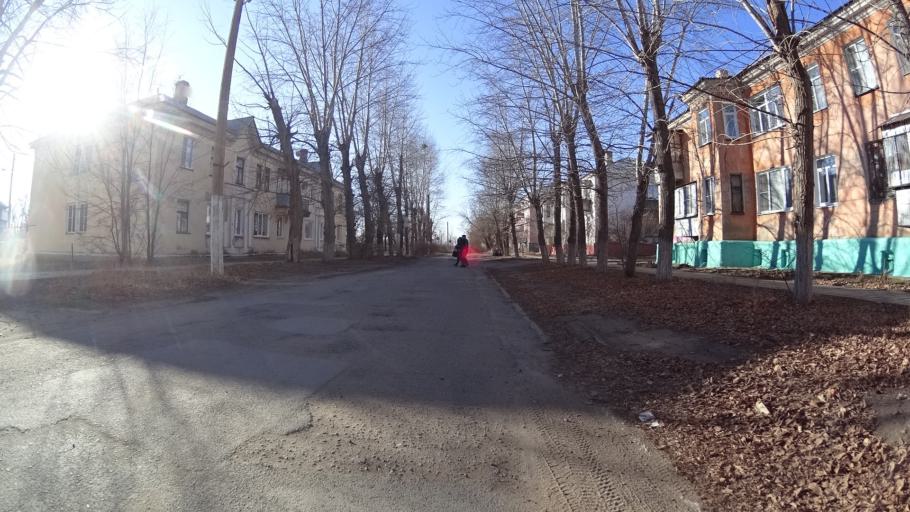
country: RU
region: Chelyabinsk
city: Troitsk
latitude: 54.0438
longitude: 61.6277
